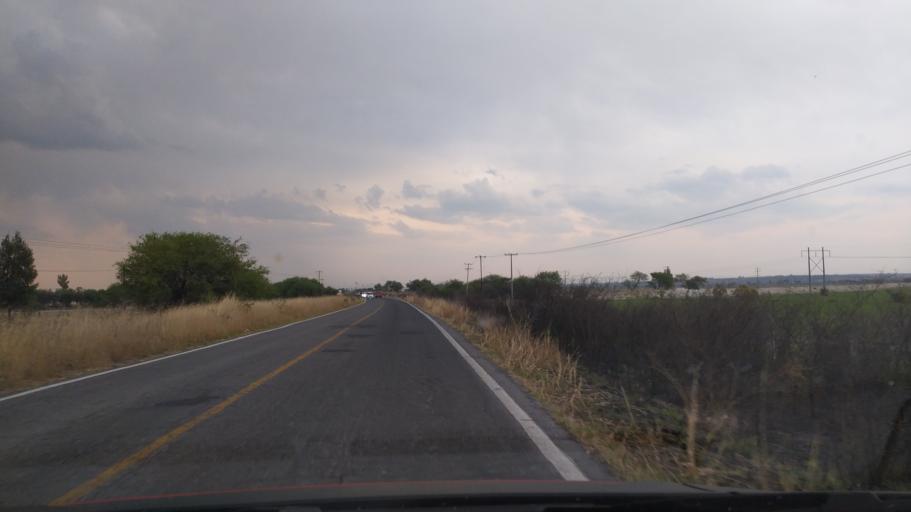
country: MX
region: Guanajuato
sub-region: San Francisco del Rincon
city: San Ignacio de Hidalgo
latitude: 20.8378
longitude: -101.8983
